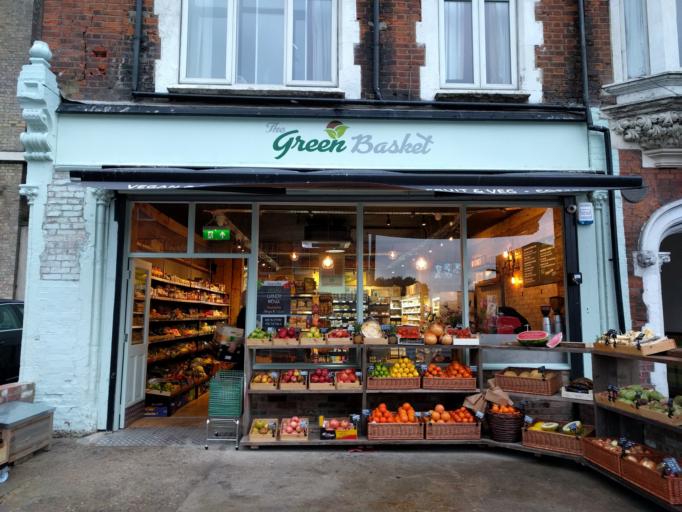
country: GB
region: England
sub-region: Greater London
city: Hackney
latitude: 51.5539
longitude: -0.0538
